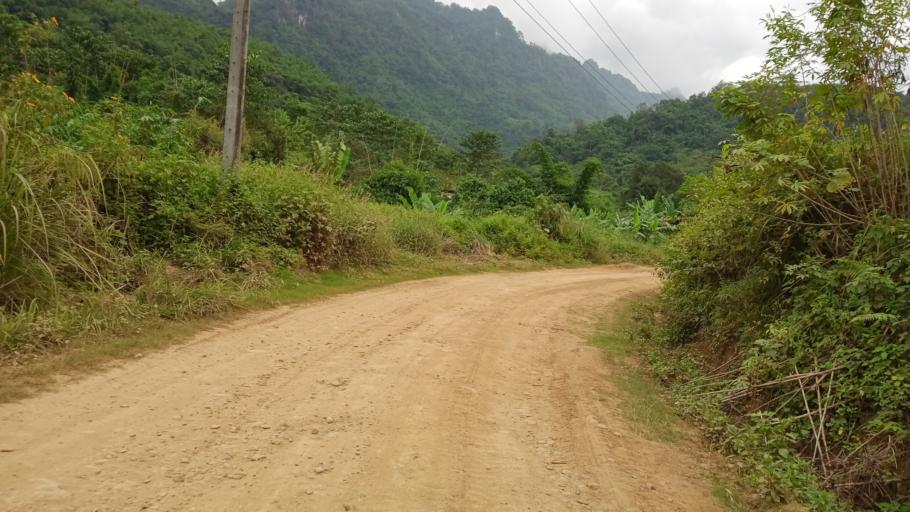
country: LA
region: Xiangkhoang
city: Phonsavan
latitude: 19.0930
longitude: 102.9939
